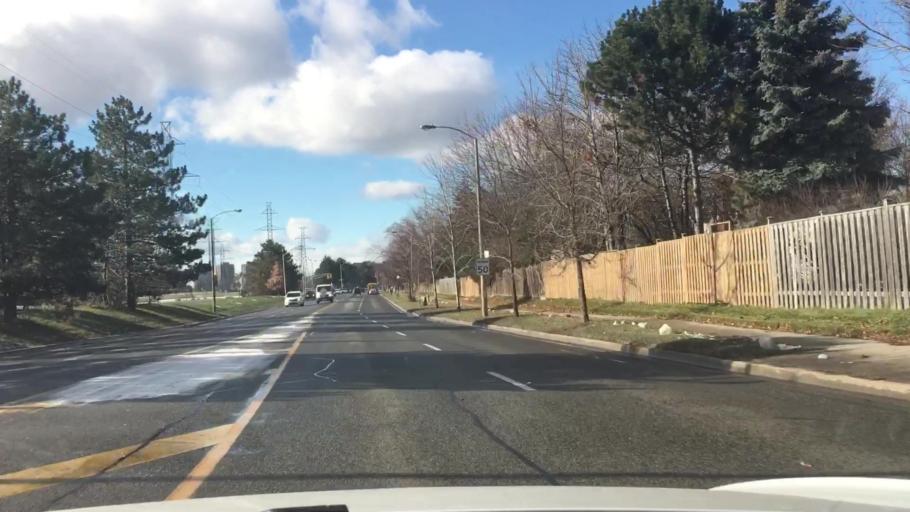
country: CA
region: Ontario
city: Scarborough
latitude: 43.8047
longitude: -79.3278
